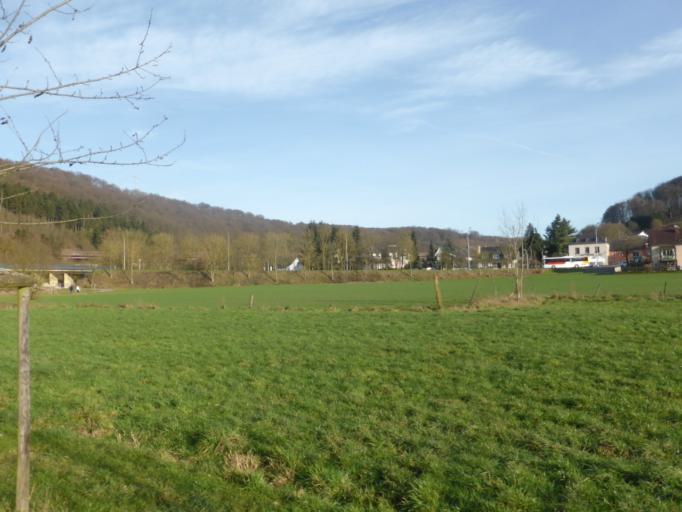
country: LU
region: Luxembourg
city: Colmar
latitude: 49.8133
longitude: 6.0953
